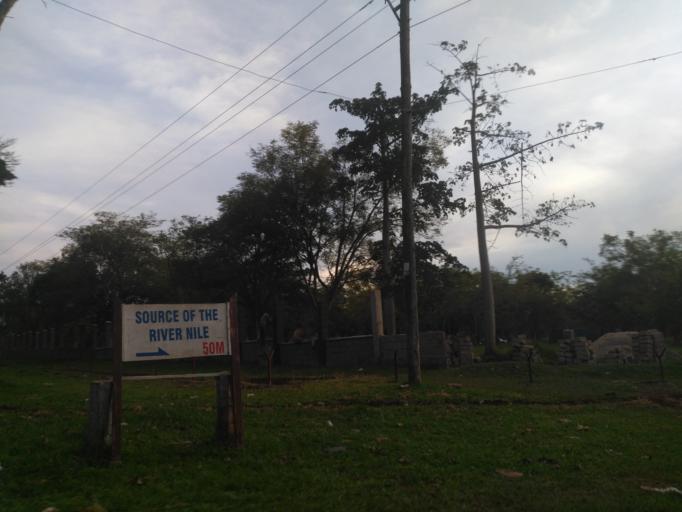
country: UG
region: Eastern Region
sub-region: Jinja District
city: Jinja
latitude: 0.4271
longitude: 33.2006
